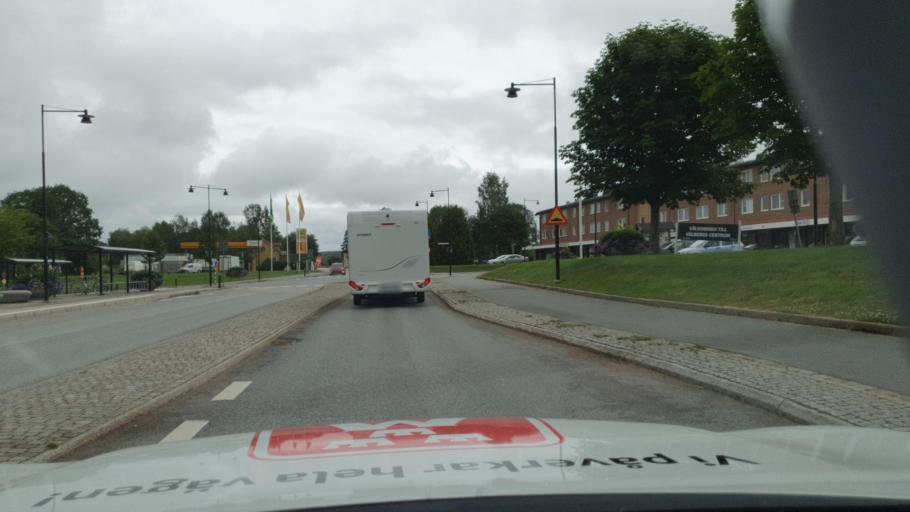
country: SE
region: Vaermland
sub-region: Karlstads Kommun
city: Valberg
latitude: 59.3950
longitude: 13.1941
